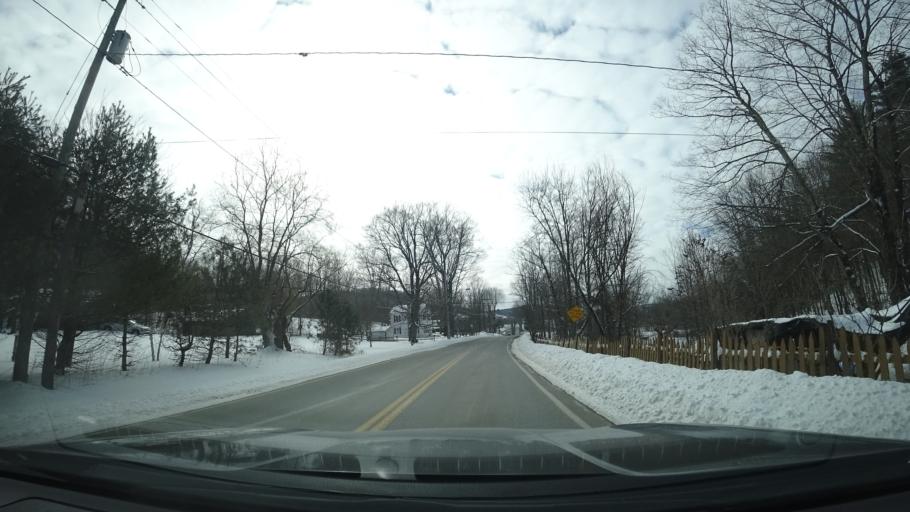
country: US
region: New York
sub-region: Washington County
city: Greenwich
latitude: 43.2325
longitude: -73.3761
